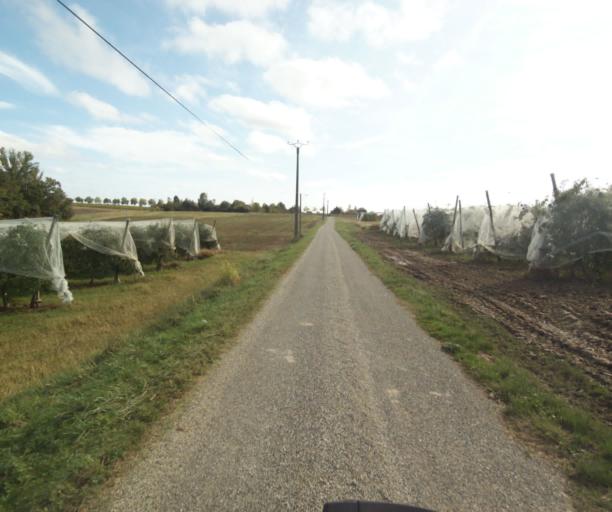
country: FR
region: Midi-Pyrenees
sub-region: Departement du Tarn-et-Garonne
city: Saint-Porquier
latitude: 43.9481
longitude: 1.1331
